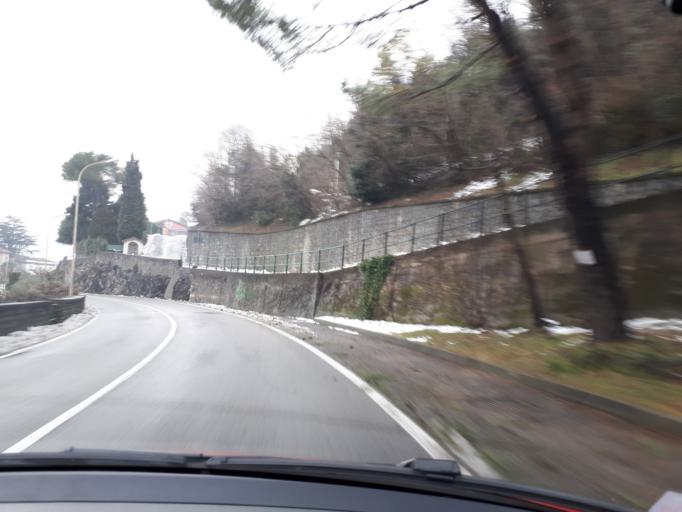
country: IT
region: Lombardy
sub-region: Provincia di Lecco
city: Mandello del Lario
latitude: 45.9296
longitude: 9.3128
